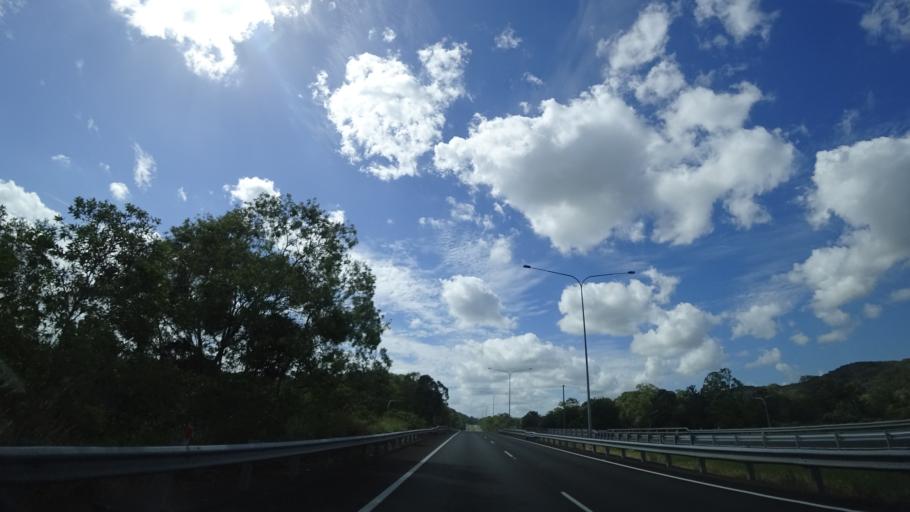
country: AU
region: Queensland
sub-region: Sunshine Coast
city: Twin Waters
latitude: -26.6162
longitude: 152.9800
